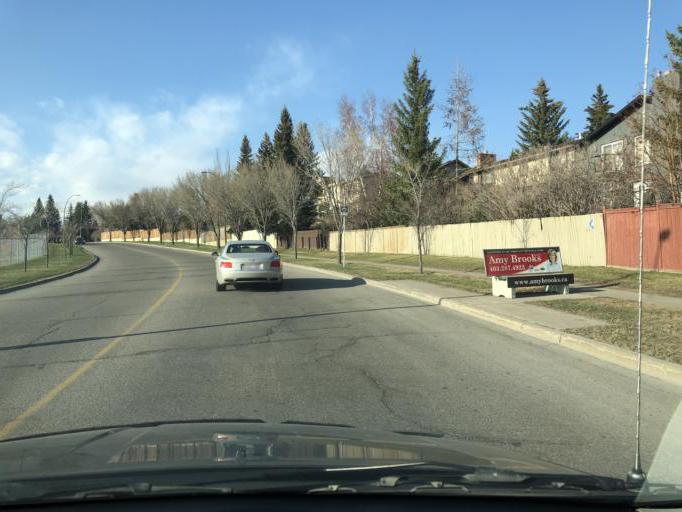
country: CA
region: Alberta
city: Calgary
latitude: 50.9635
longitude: -114.1021
